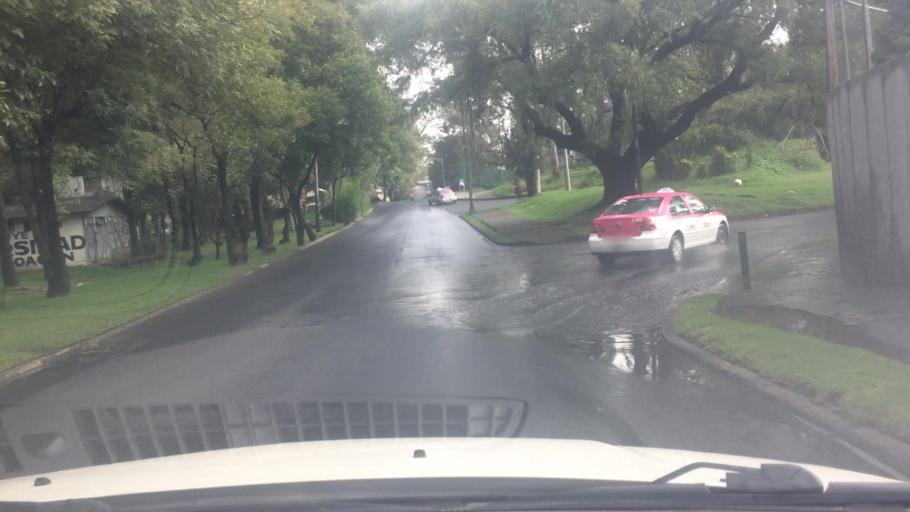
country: MX
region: Mexico City
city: Colonia Nativitas
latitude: 19.3513
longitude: -99.1300
